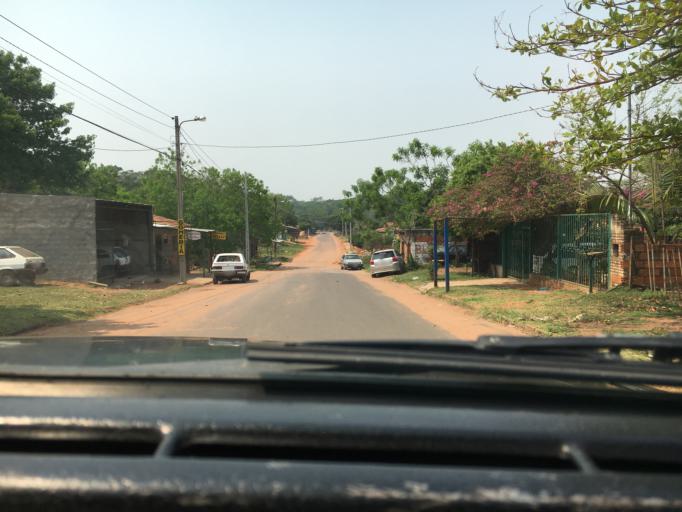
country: PY
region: Central
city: Villa Elisa
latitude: -25.3830
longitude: -57.5736
